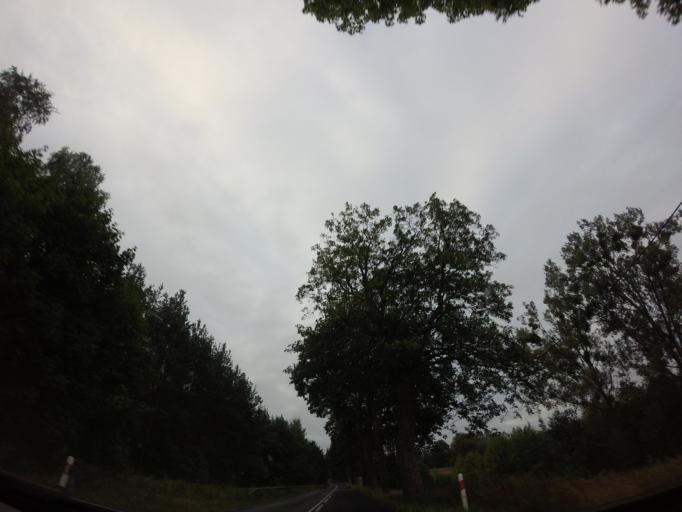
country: PL
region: Lubusz
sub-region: Powiat strzelecko-drezdenecki
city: Dobiegniew
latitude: 52.9348
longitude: 15.7511
